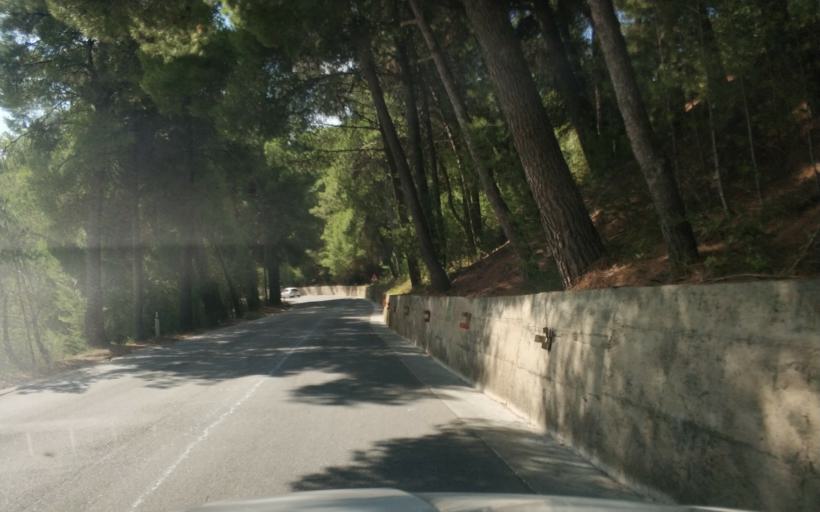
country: AL
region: Durres
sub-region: Rrethi i Krujes
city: Kruje
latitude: 41.4977
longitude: 19.7761
